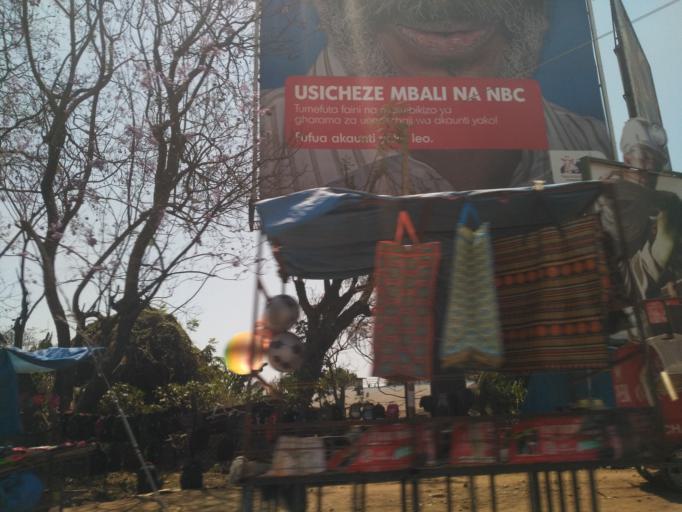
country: TZ
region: Arusha
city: Arusha
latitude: -3.3626
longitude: 36.6836
